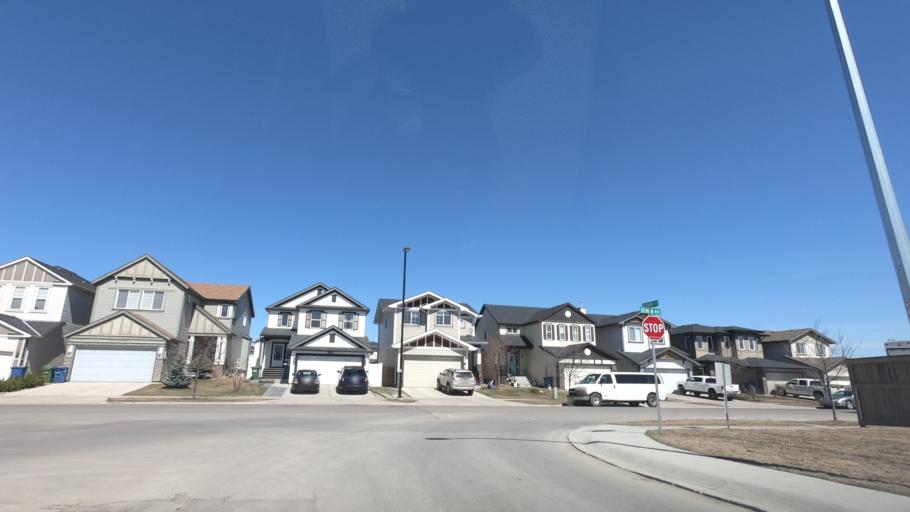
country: CA
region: Alberta
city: Airdrie
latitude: 51.3029
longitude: -114.0444
